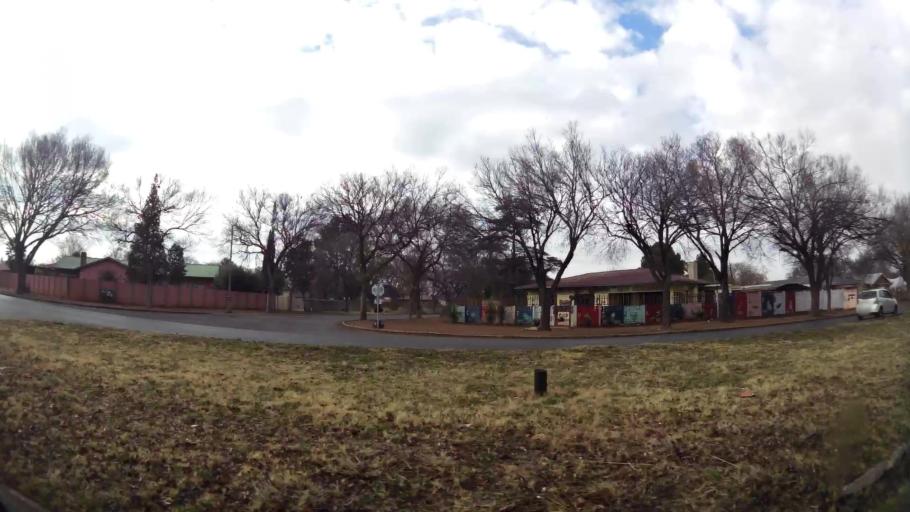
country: ZA
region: Gauteng
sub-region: Sedibeng District Municipality
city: Vanderbijlpark
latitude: -26.6909
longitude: 27.8234
